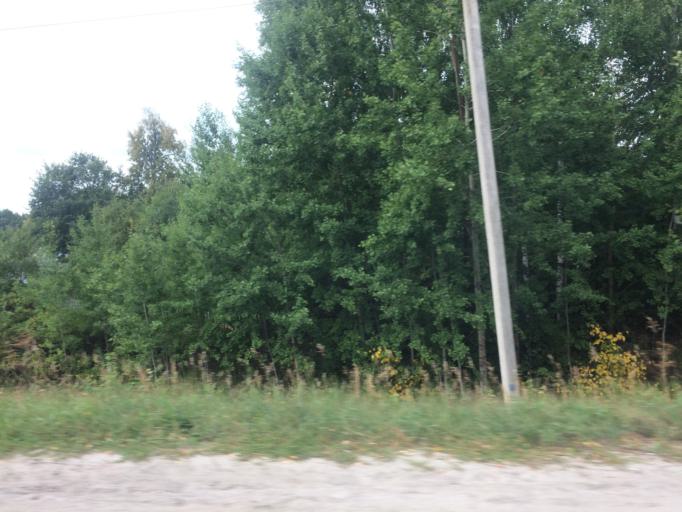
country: RU
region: Mariy-El
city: Yoshkar-Ola
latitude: 56.5590
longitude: 47.9809
